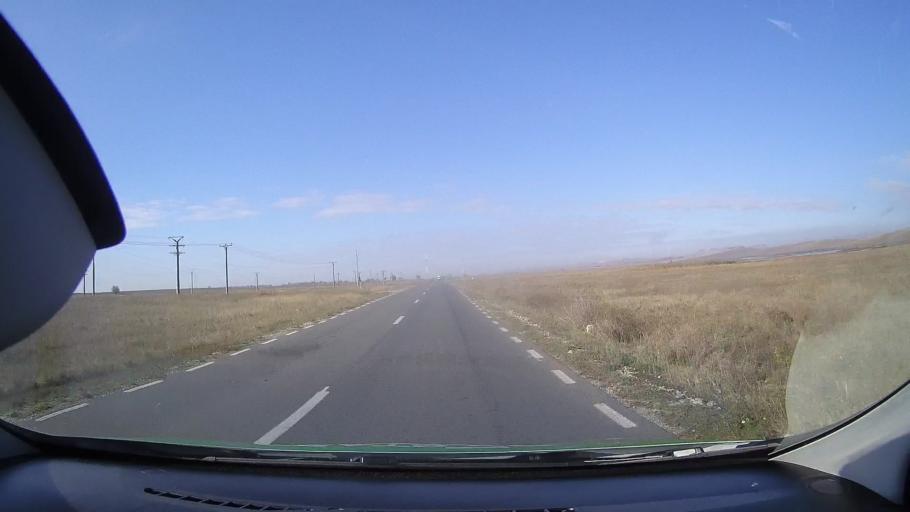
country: RO
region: Tulcea
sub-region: Comuna Murighiol
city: Murighiol
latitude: 45.0279
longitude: 29.1552
